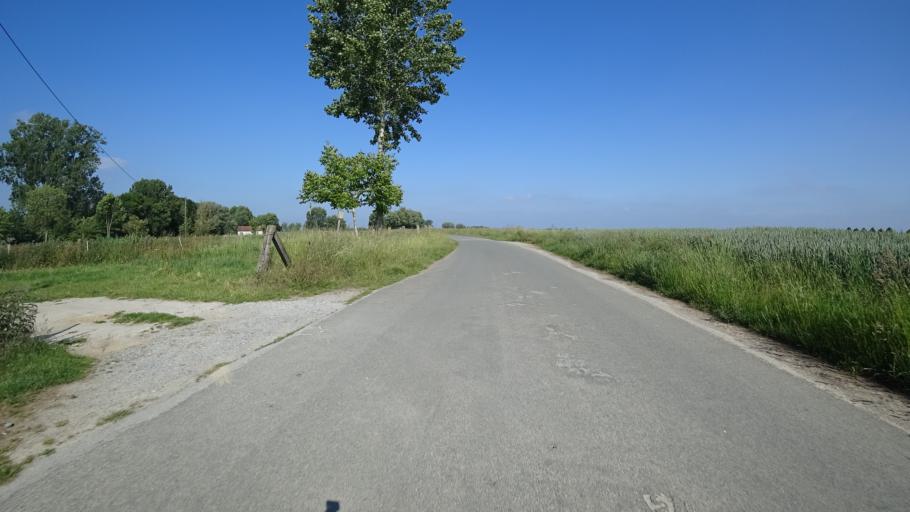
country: DE
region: North Rhine-Westphalia
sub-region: Regierungsbezirk Arnsberg
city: Lippstadt
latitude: 51.6388
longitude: 8.3863
